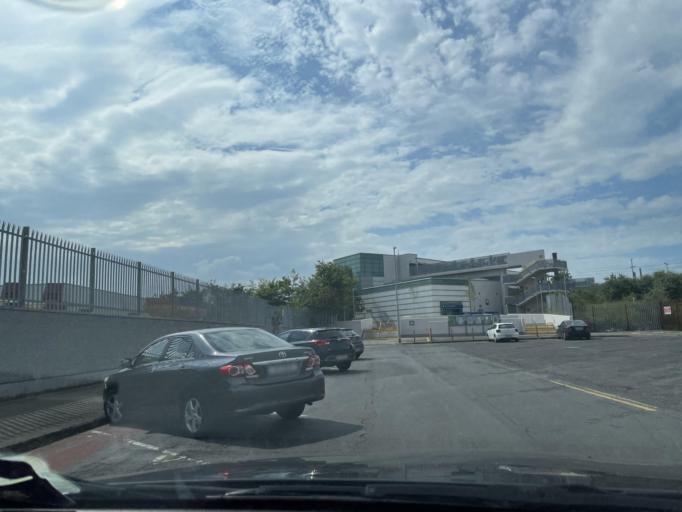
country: IE
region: Leinster
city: Donaghmede
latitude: 53.3910
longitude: -6.1540
